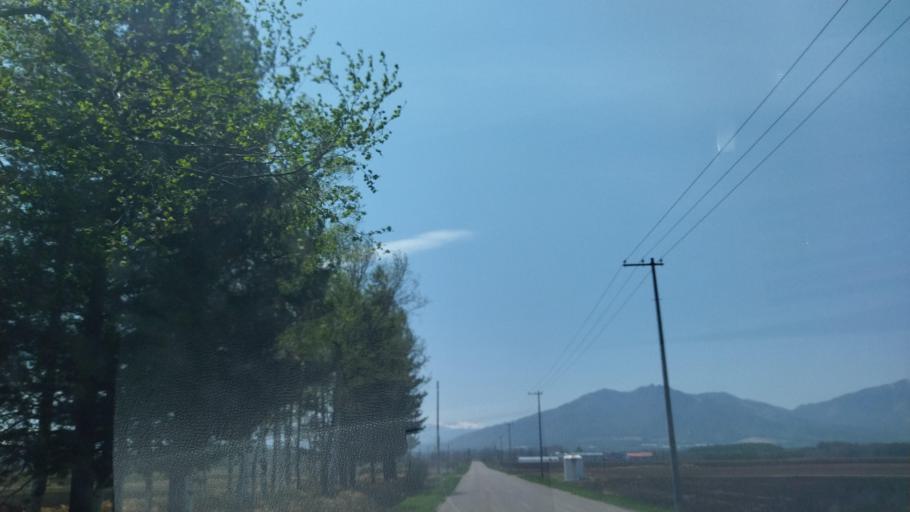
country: JP
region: Hokkaido
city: Obihiro
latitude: 42.9038
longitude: 142.9861
